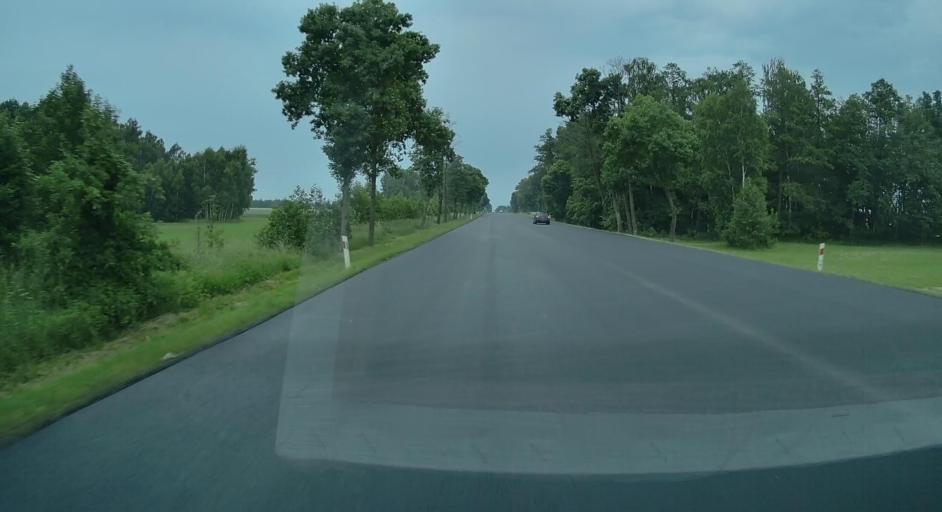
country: PL
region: Lublin Voivodeship
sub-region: Powiat lukowski
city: Trzebieszow
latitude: 52.0552
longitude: 22.6407
